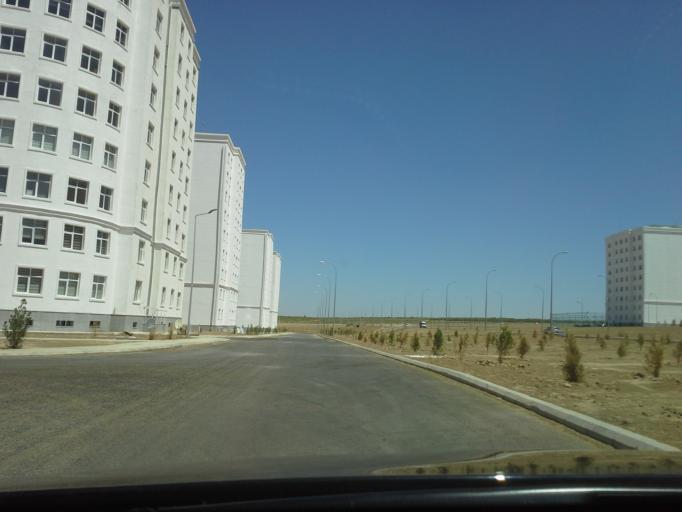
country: TM
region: Ahal
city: Ashgabat
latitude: 37.8906
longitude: 58.4094
